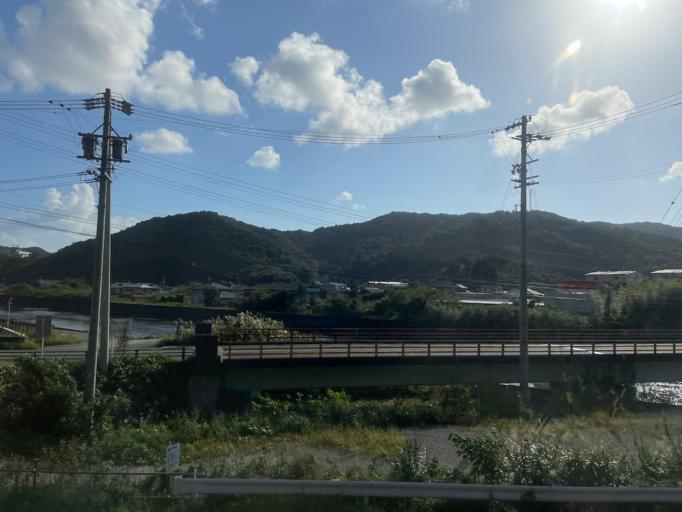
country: JP
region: Mie
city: Toba
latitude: 34.4607
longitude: 136.8414
